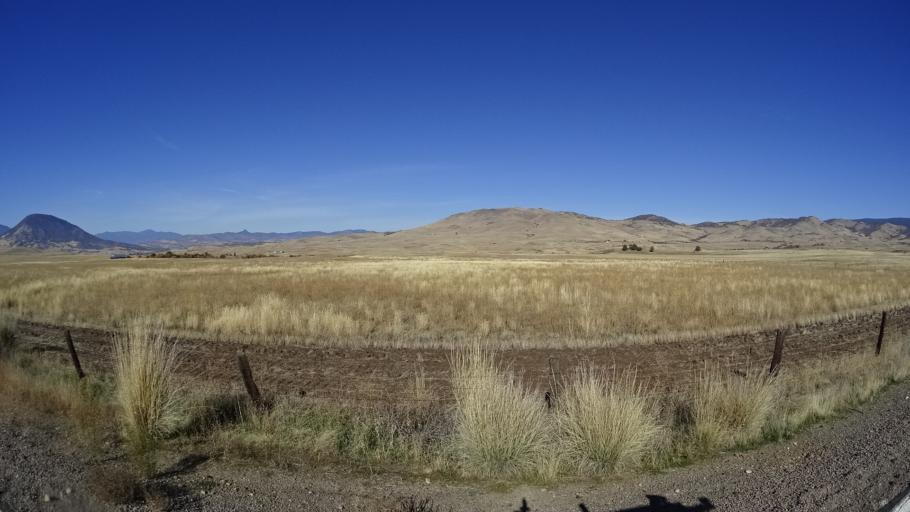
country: US
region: California
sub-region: Siskiyou County
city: Montague
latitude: 41.8044
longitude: -122.4070
